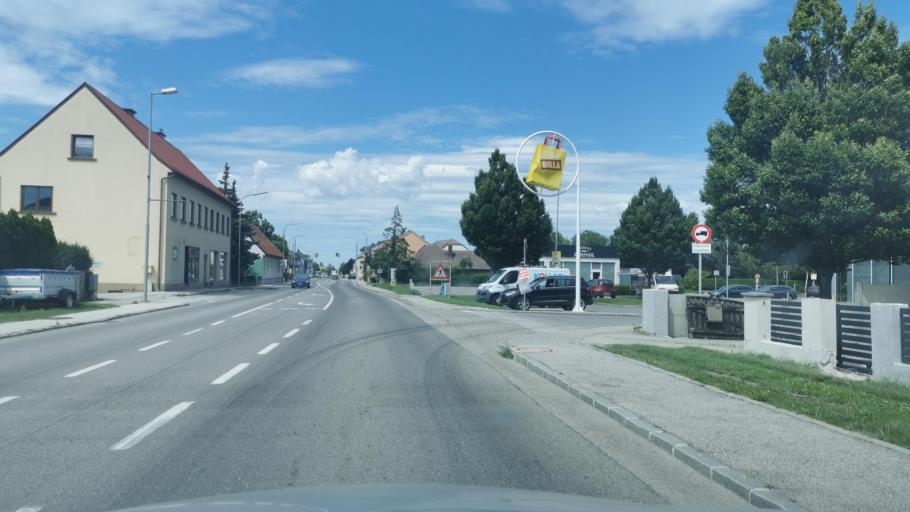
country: AT
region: Lower Austria
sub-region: Politischer Bezirk Sankt Polten
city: Wilhelmsburg
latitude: 48.1368
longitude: 15.6133
